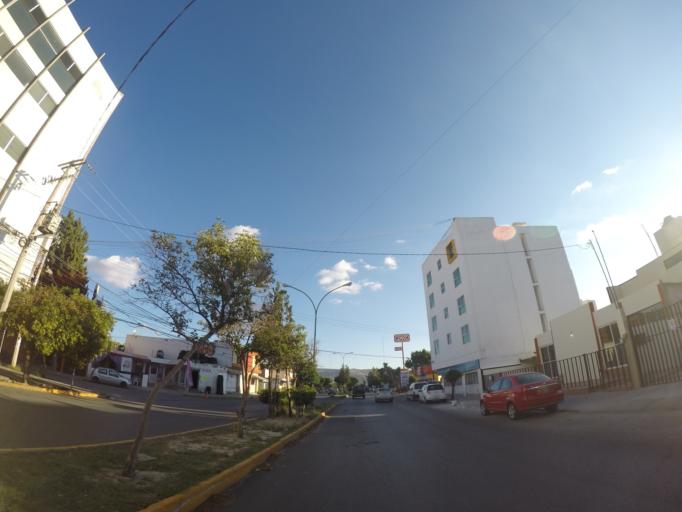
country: MX
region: San Luis Potosi
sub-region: San Luis Potosi
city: San Luis Potosi
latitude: 22.1461
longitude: -100.9843
